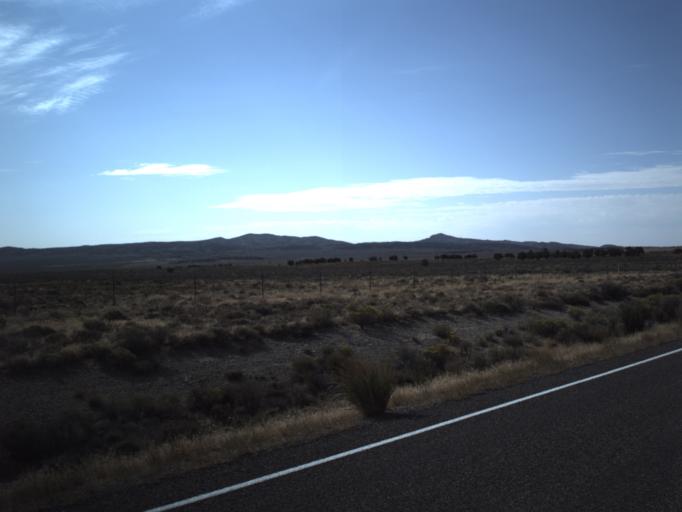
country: US
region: Idaho
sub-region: Cassia County
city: Burley
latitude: 41.7239
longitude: -113.5254
